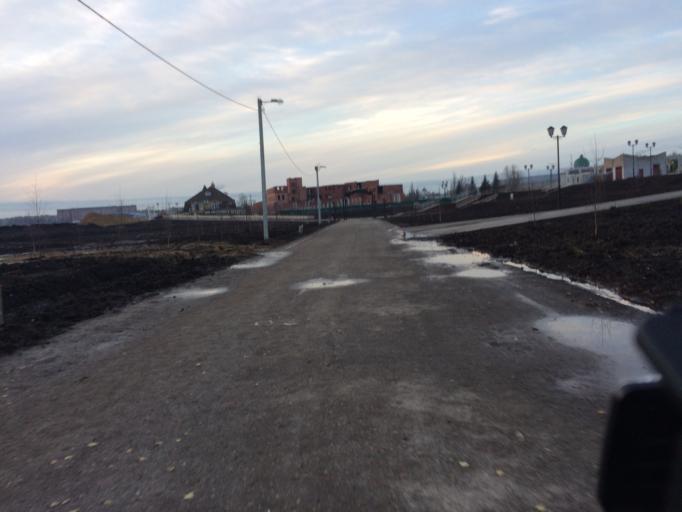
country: RU
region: Mariy-El
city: Yoshkar-Ola
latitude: 56.6255
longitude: 47.9082
